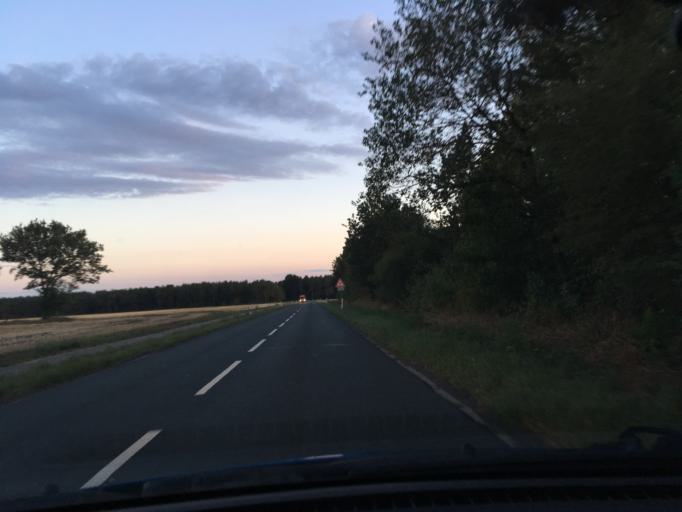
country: DE
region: Lower Saxony
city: Fassberg
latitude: 52.9245
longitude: 10.1520
